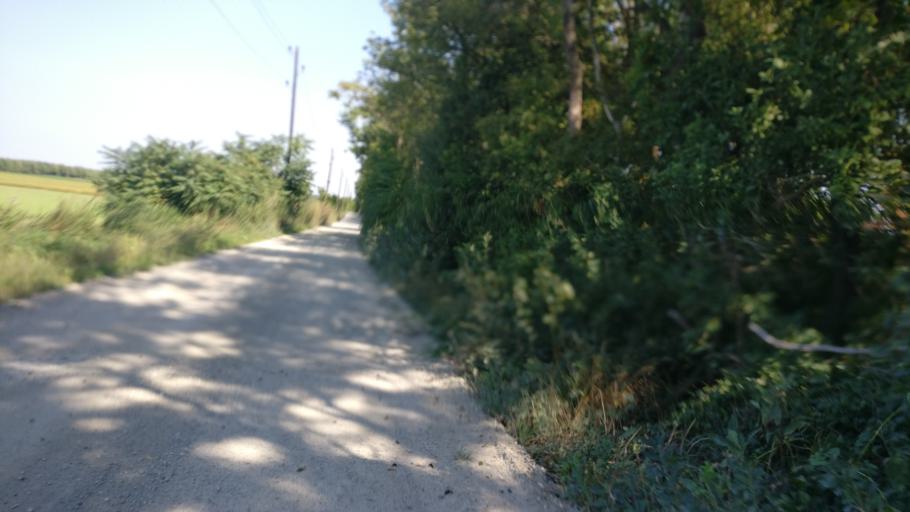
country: AT
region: Lower Austria
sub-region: Politischer Bezirk Baden
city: Ebreichsdorf
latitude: 47.9789
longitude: 16.4036
